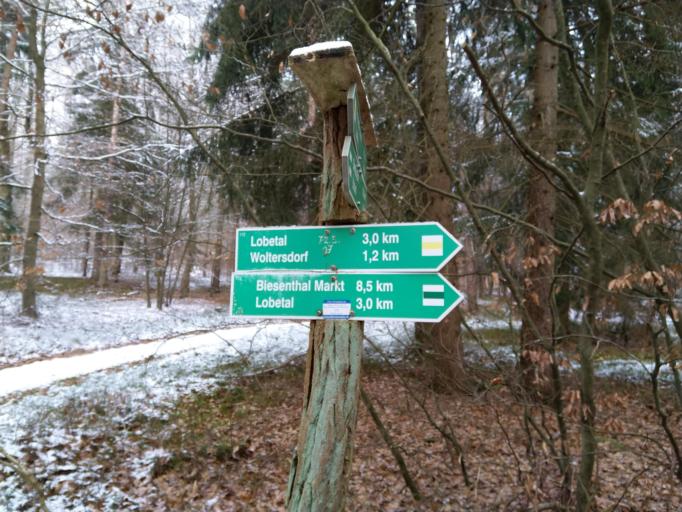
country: DE
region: Brandenburg
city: Bernau bei Berlin
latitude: 52.7388
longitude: 13.5598
